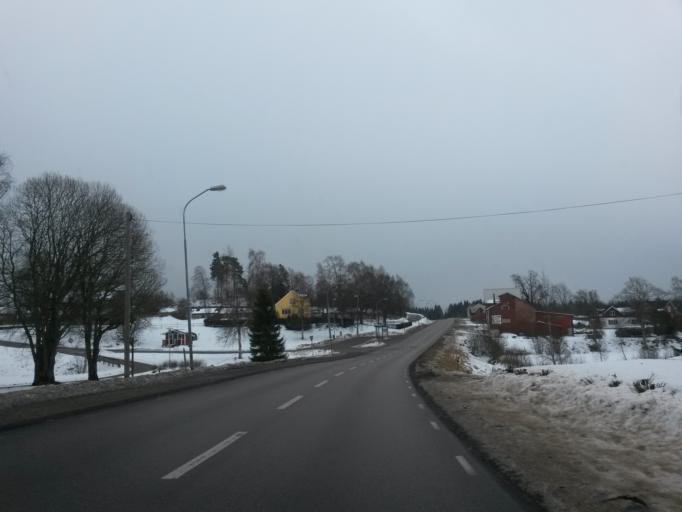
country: SE
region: Vaestra Goetaland
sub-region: Ulricehamns Kommun
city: Ulricehamn
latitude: 57.8992
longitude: 13.3494
